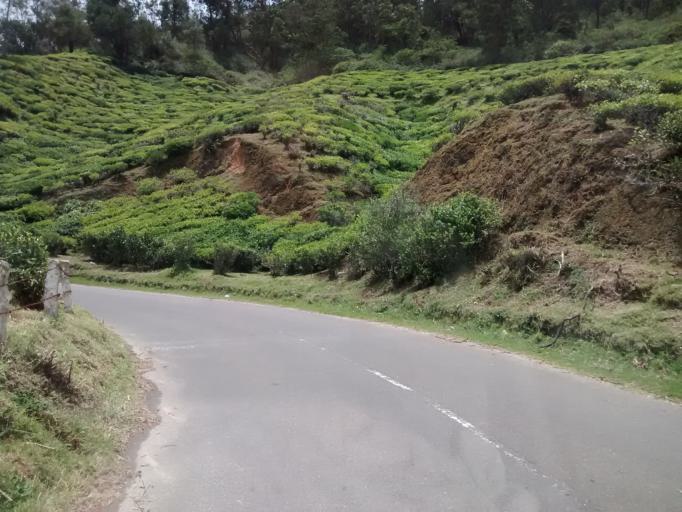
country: IN
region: Kerala
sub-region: Idukki
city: Munnar
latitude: 10.1398
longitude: 77.1971
